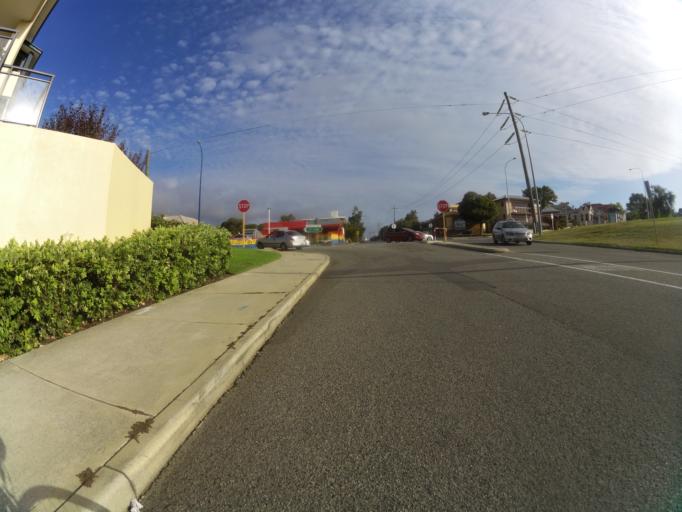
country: AU
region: Western Australia
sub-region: East Fremantle
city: East Fremantle
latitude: -32.0419
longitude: 115.7581
